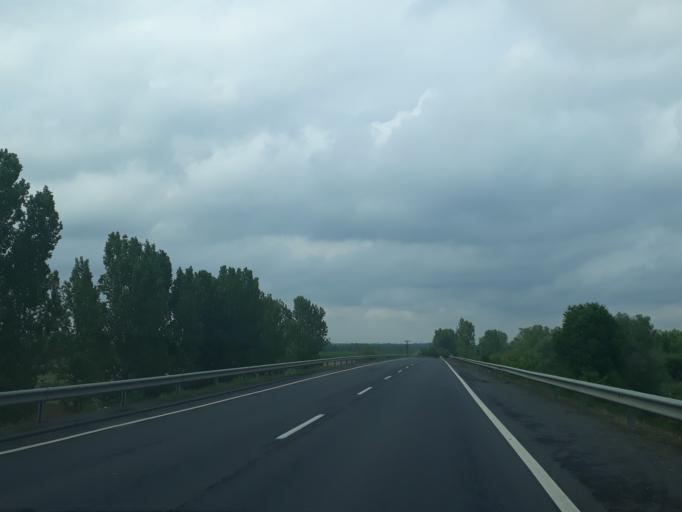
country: HU
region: Szabolcs-Szatmar-Bereg
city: Ajak
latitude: 48.1844
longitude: 22.0420
